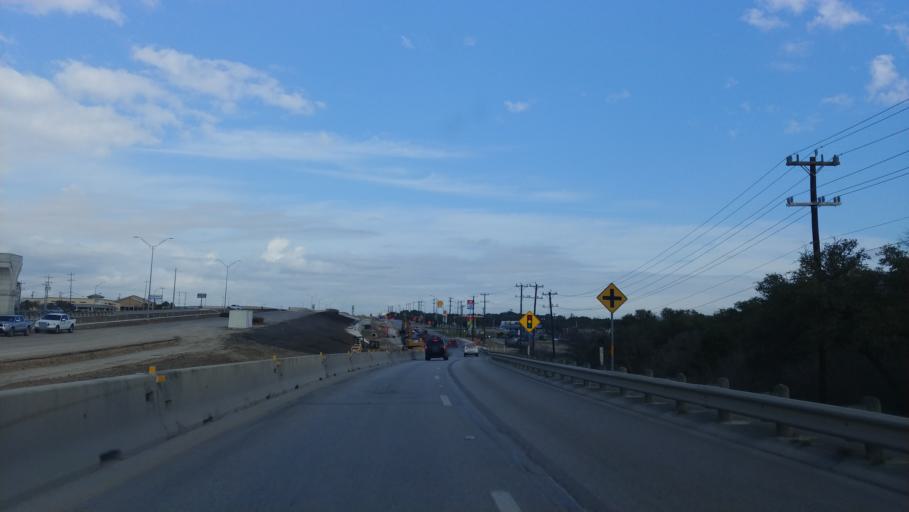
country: US
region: Texas
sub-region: Bexar County
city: Leon Valley
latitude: 29.4446
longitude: -98.7109
